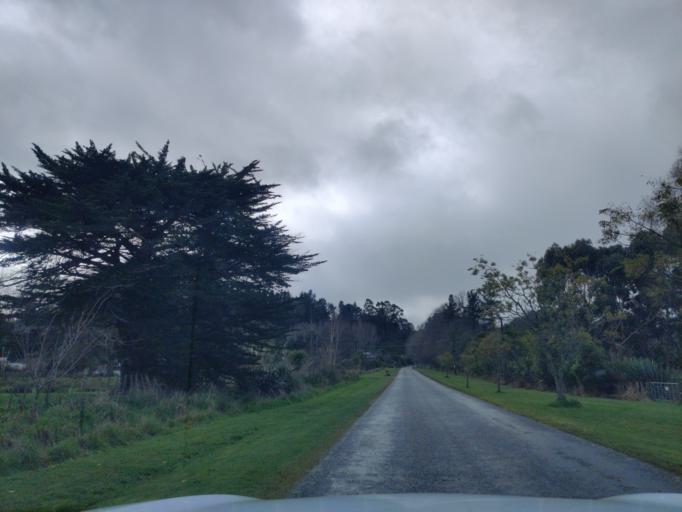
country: NZ
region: Manawatu-Wanganui
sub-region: Palmerston North City
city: Palmerston North
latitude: -40.1702
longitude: 175.7993
